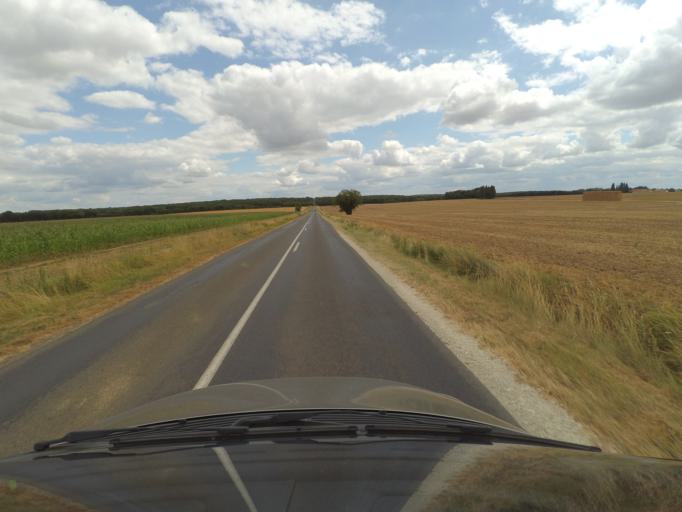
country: FR
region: Poitou-Charentes
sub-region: Departement de la Vienne
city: Saint-Savin
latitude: 46.5622
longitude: 0.8956
